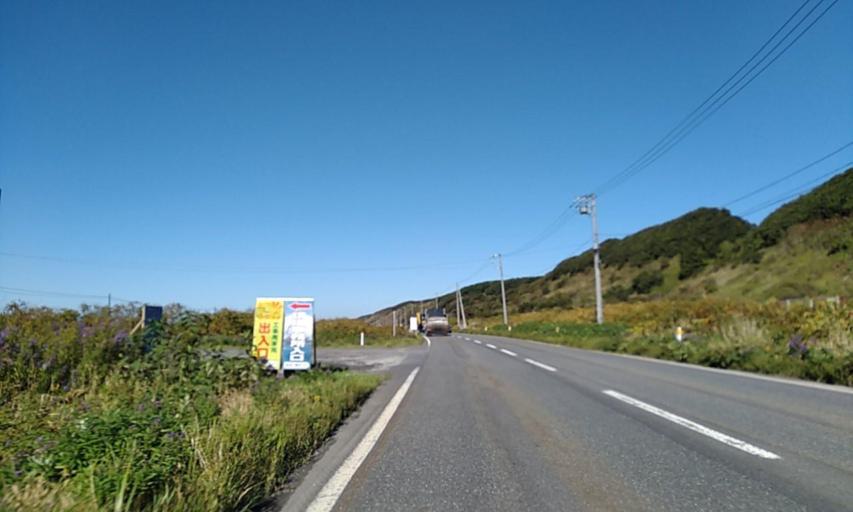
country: JP
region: Hokkaido
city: Shizunai-furukawacho
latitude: 42.4625
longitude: 142.1612
